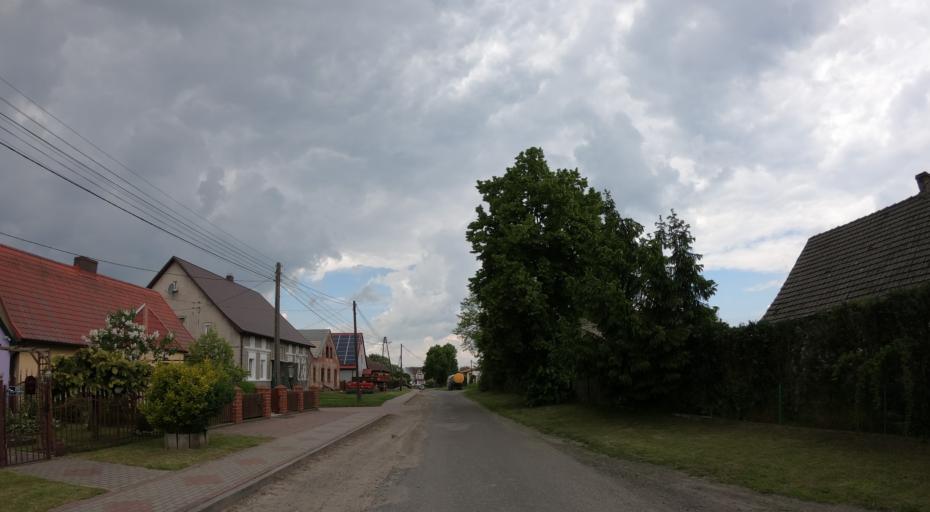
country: PL
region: West Pomeranian Voivodeship
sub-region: Powiat pyrzycki
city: Kozielice
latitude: 53.1511
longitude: 14.7909
